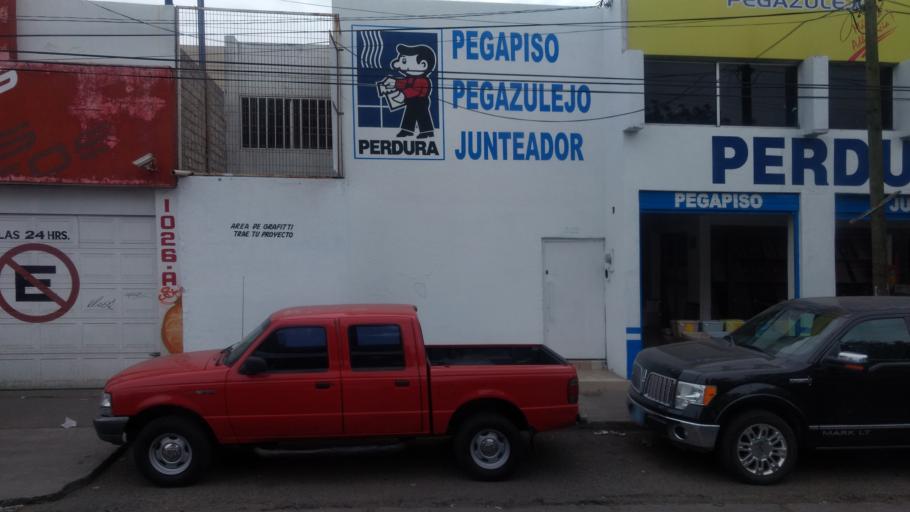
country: MX
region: Guanajuato
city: Leon
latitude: 21.1419
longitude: -101.6744
